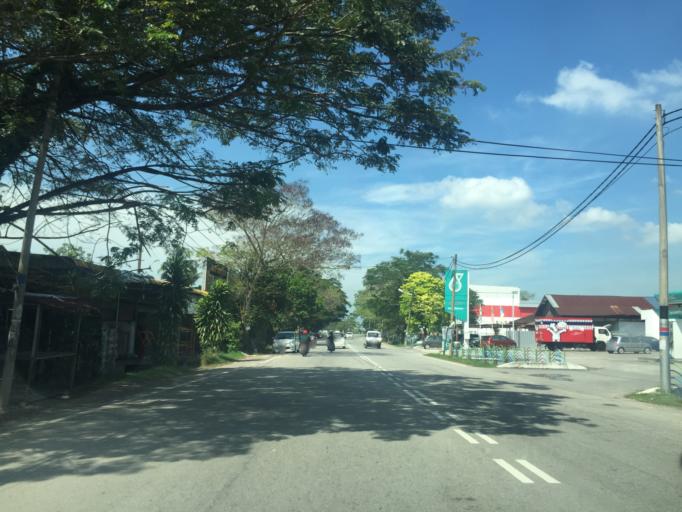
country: MY
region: Penang
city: Tasek Glugor
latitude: 5.4842
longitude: 100.4888
